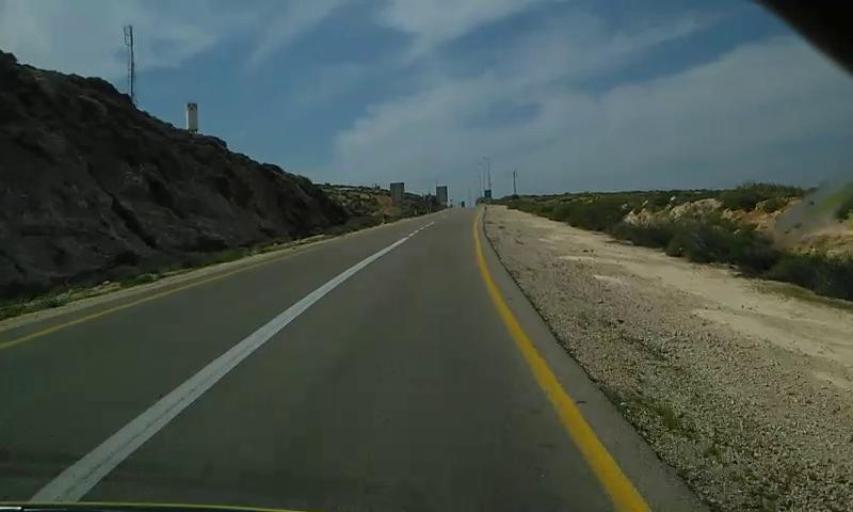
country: PS
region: West Bank
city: Az Zahiriyah
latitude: 31.3745
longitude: 35.0103
